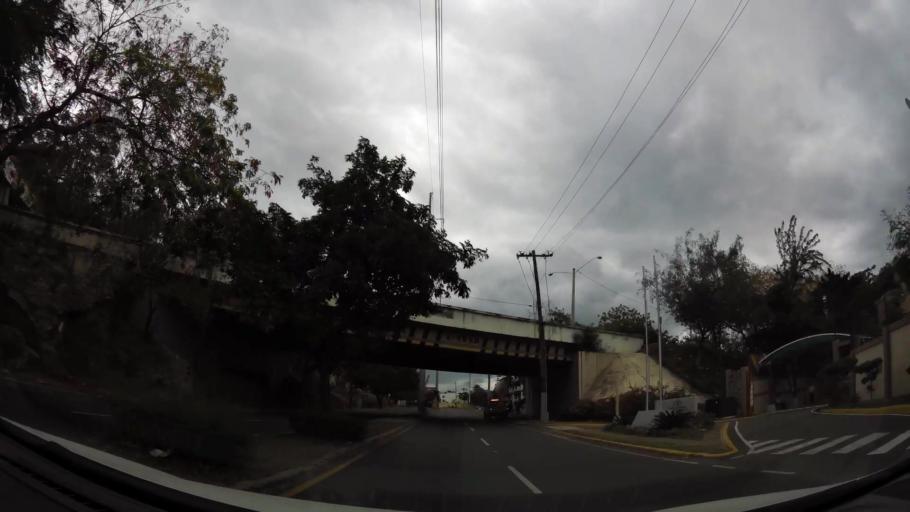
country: DO
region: Nacional
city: Bella Vista
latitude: 18.4437
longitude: -69.9477
